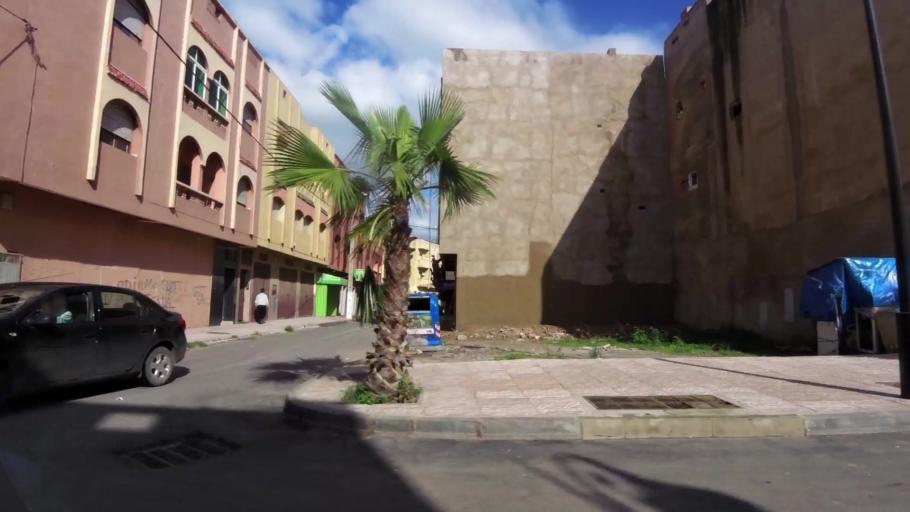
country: MA
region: Chaouia-Ouardigha
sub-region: Settat Province
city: Berrechid
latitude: 33.2625
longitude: -7.5713
